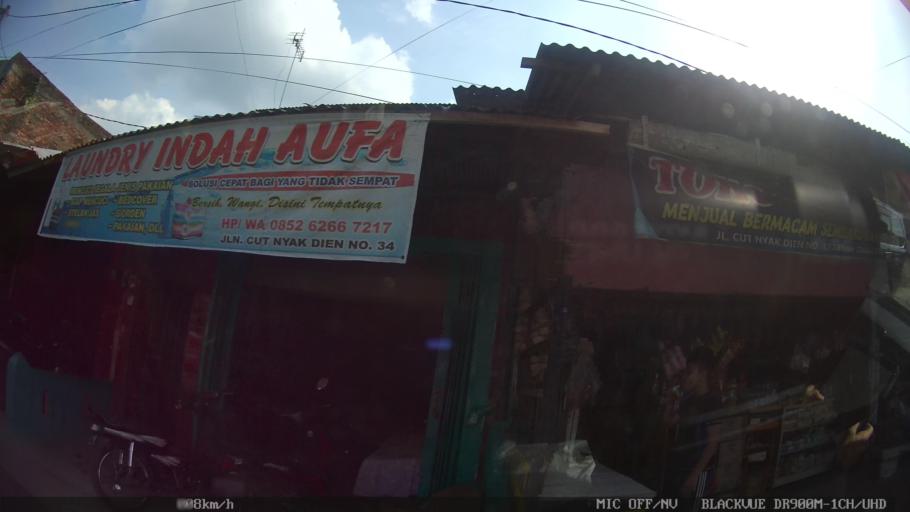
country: ID
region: North Sumatra
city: Binjai
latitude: 3.6104
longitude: 98.4980
